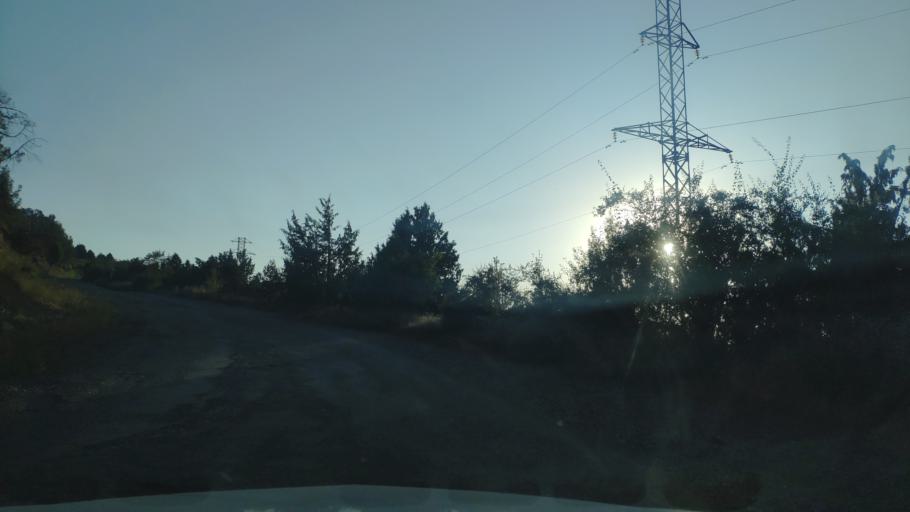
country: TJ
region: Viloyati Sughd
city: Ayni
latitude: 39.6391
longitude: 68.4683
